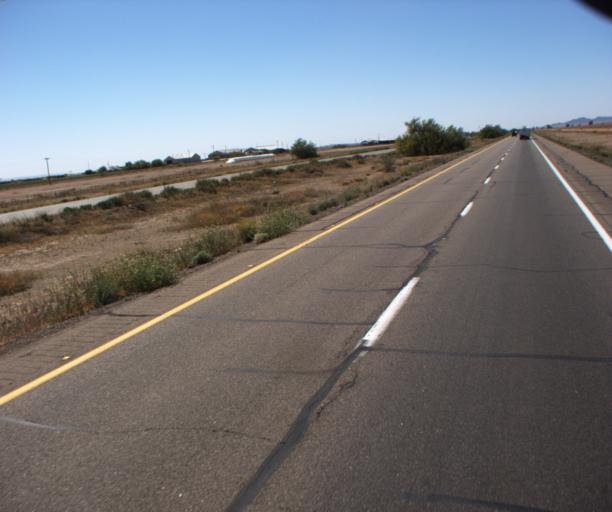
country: US
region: Arizona
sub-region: Maricopa County
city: Gila Bend
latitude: 32.9265
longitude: -112.8542
